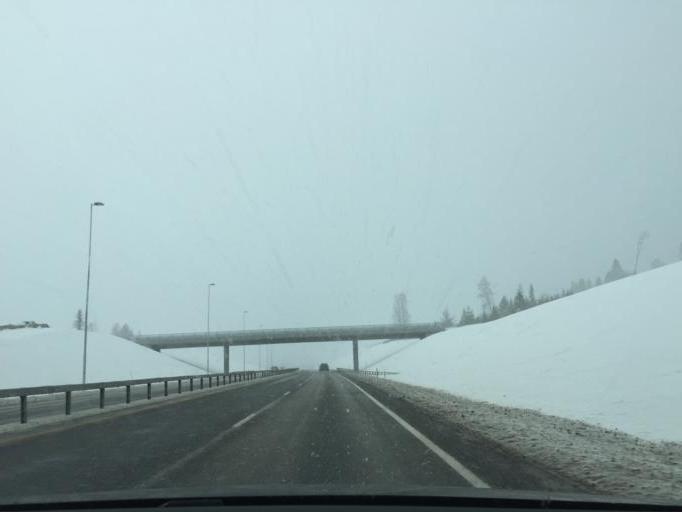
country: NO
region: Hedmark
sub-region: Sor-Odal
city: Skarnes
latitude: 60.2416
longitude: 11.7912
